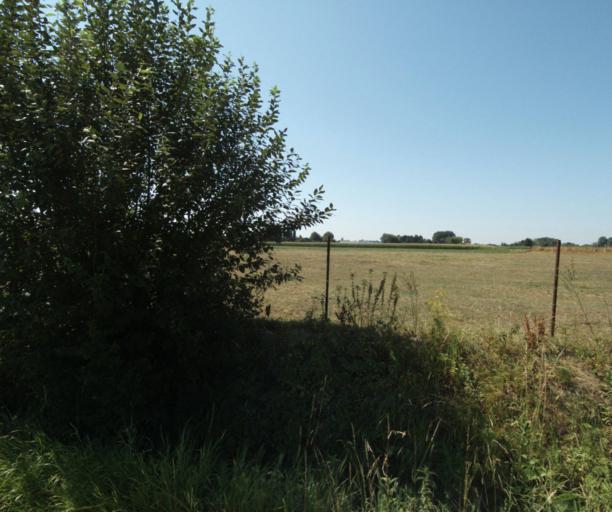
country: FR
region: Nord-Pas-de-Calais
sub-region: Departement du Nord
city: Bousbecque
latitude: 50.7568
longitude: 3.0970
